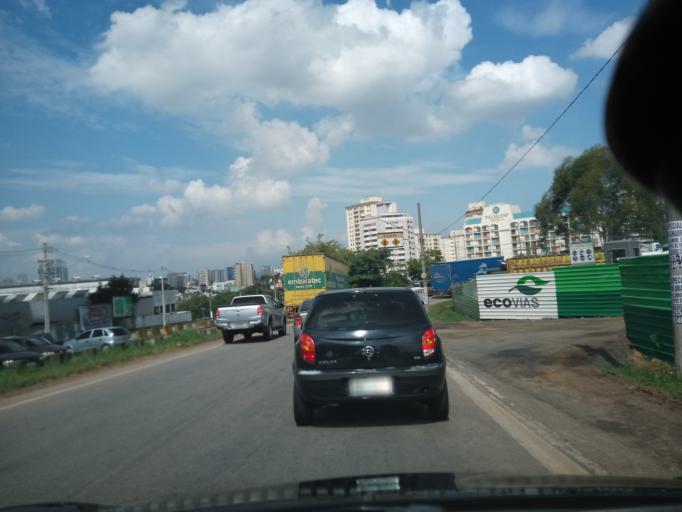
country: BR
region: Sao Paulo
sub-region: Sao Bernardo Do Campo
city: Sao Bernardo do Campo
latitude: -23.6883
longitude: -46.5644
